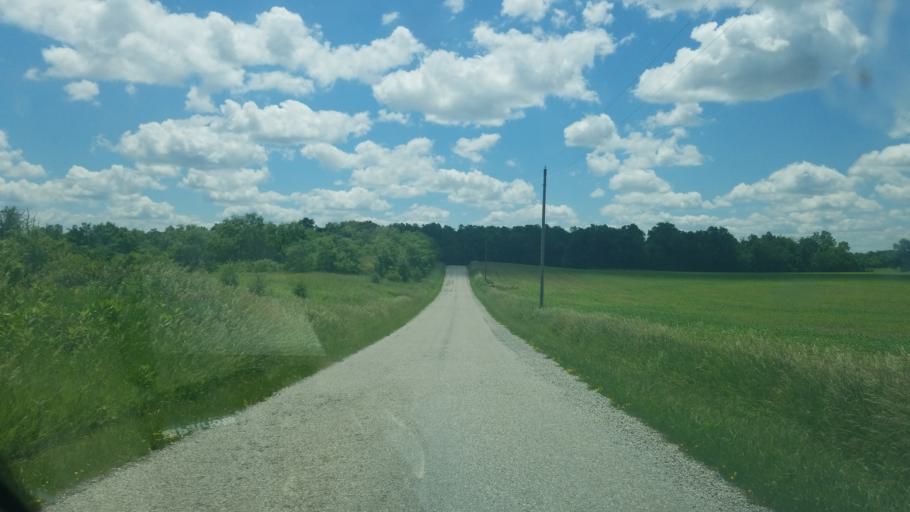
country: US
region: Ohio
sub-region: Ashland County
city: Ashland
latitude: 40.9835
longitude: -82.3266
